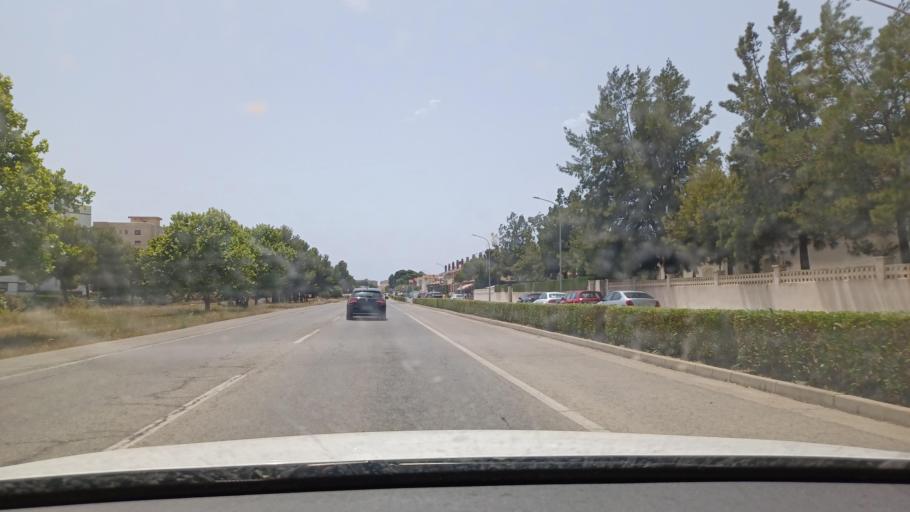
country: ES
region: Catalonia
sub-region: Provincia de Tarragona
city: Vilanova d'Escornalbou
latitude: 41.0196
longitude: 0.9519
